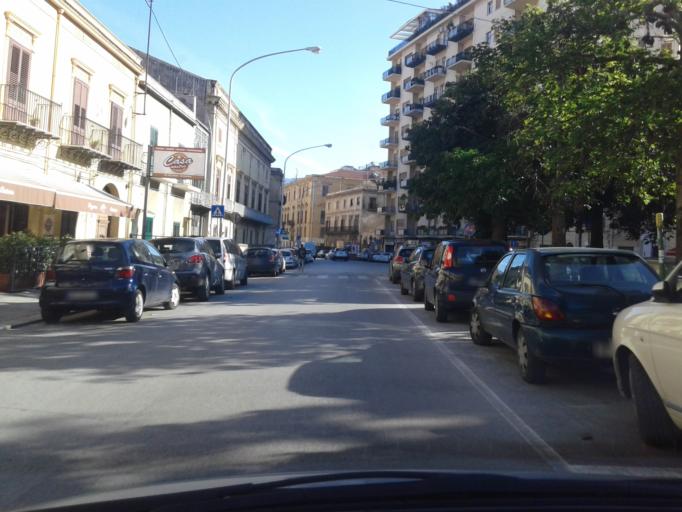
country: IT
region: Sicily
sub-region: Palermo
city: Palermo
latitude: 38.1196
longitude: 13.3415
